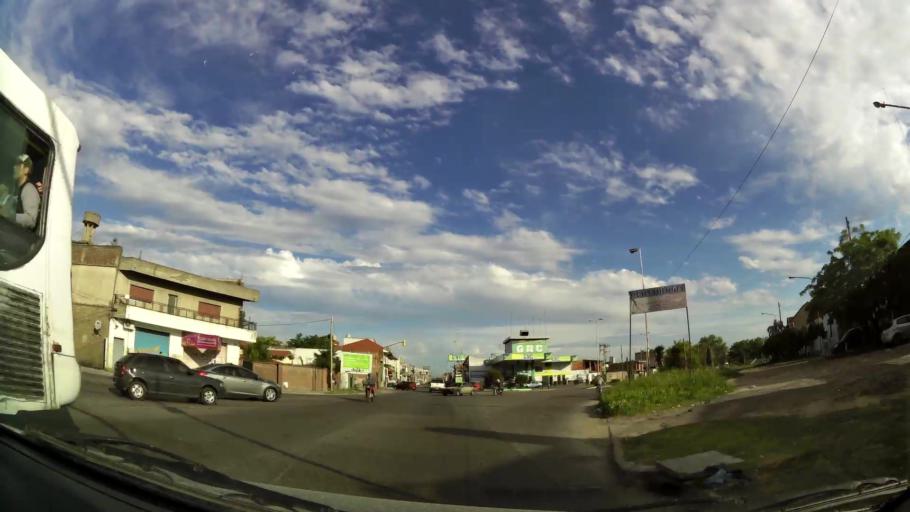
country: AR
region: Buenos Aires
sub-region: Partido de Lanus
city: Lanus
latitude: -34.7105
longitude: -58.3525
